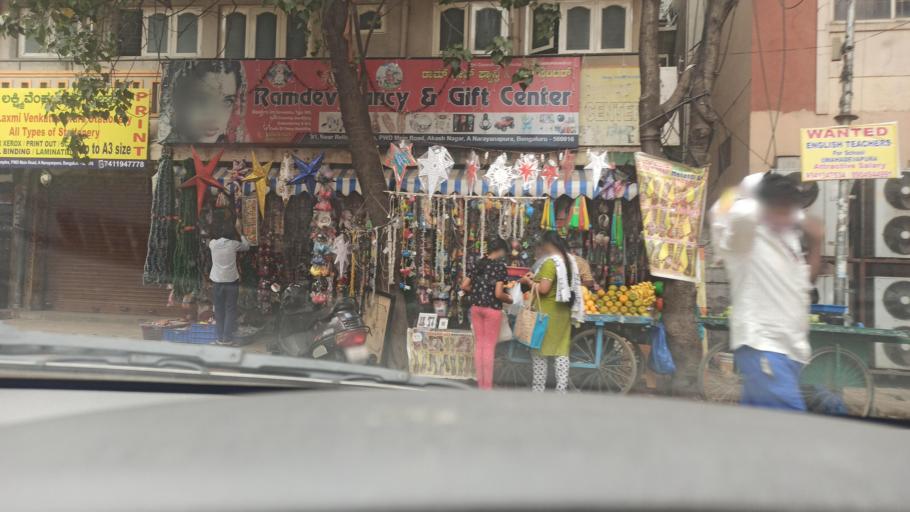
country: IN
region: Karnataka
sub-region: Bangalore Urban
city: Bangalore
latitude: 12.9928
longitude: 77.6804
